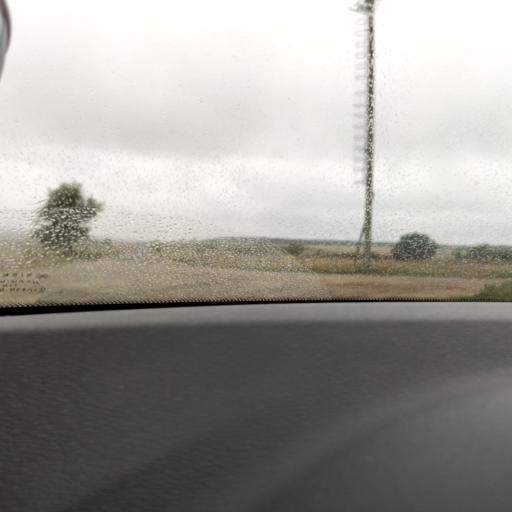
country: RU
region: Samara
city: Yelkhovka
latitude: 53.7451
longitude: 50.2417
